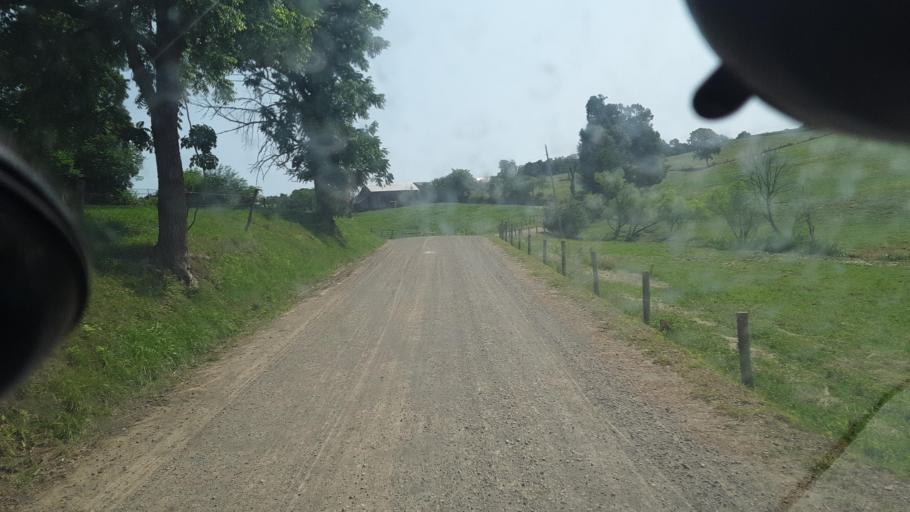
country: US
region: Ohio
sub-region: Holmes County
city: Millersburg
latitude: 40.4344
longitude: -81.8449
